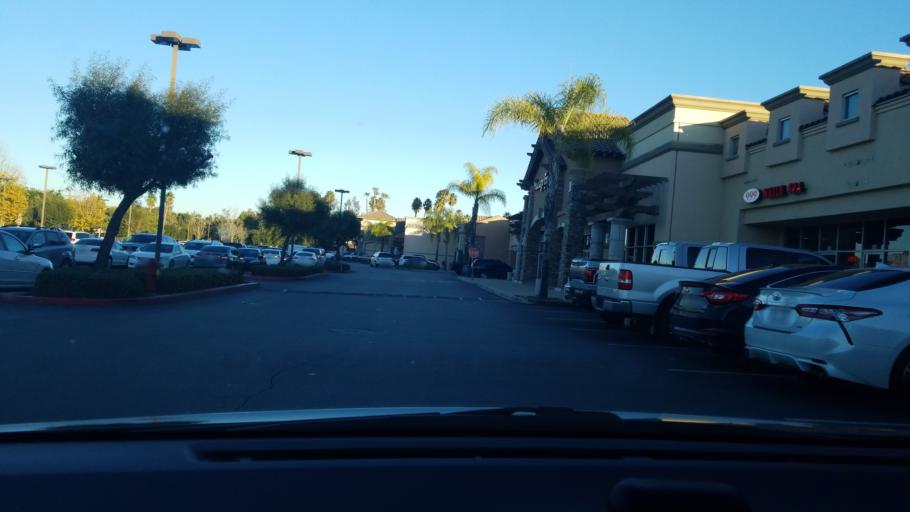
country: US
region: California
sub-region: Riverside County
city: Murrieta Hot Springs
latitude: 33.5553
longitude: -117.1563
